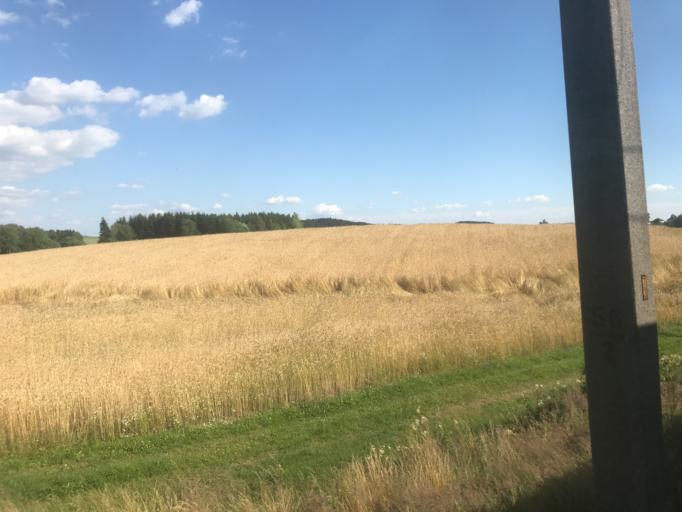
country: AT
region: Upper Austria
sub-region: Politischer Bezirk Freistadt
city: Freistadt
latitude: 48.5597
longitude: 14.4577
